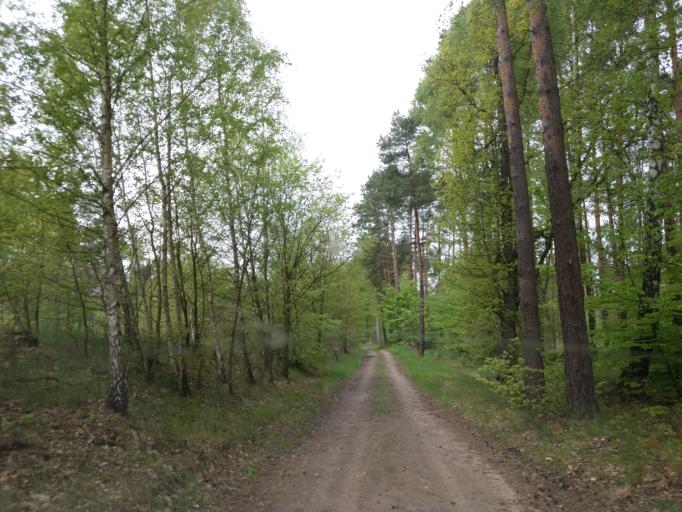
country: PL
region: West Pomeranian Voivodeship
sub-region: Powiat choszczenski
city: Bierzwnik
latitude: 53.0113
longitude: 15.6859
